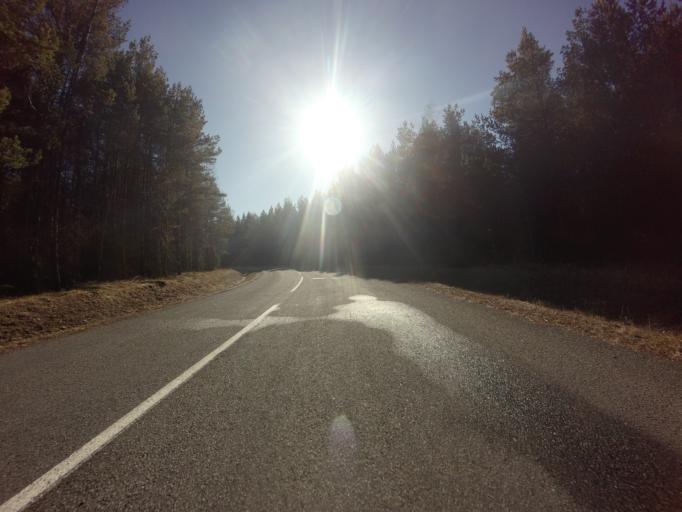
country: EE
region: Saare
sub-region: Kuressaare linn
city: Kuressaare
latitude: 58.5107
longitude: 22.3138
